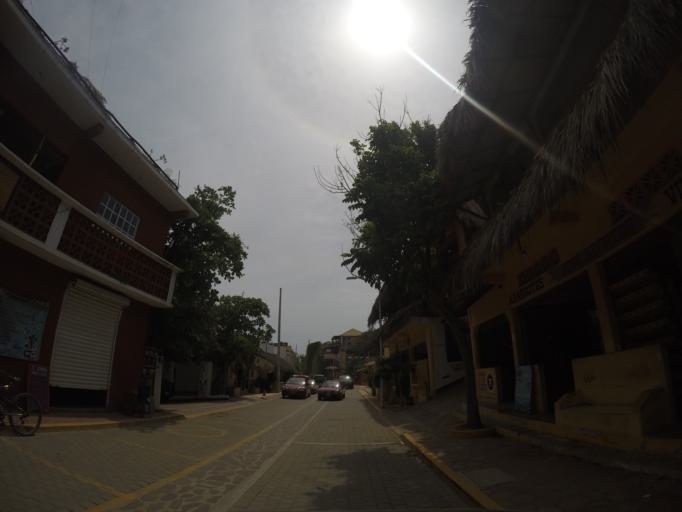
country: MX
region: Oaxaca
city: Santa Maria Tonameca
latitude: 15.6660
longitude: -96.5428
